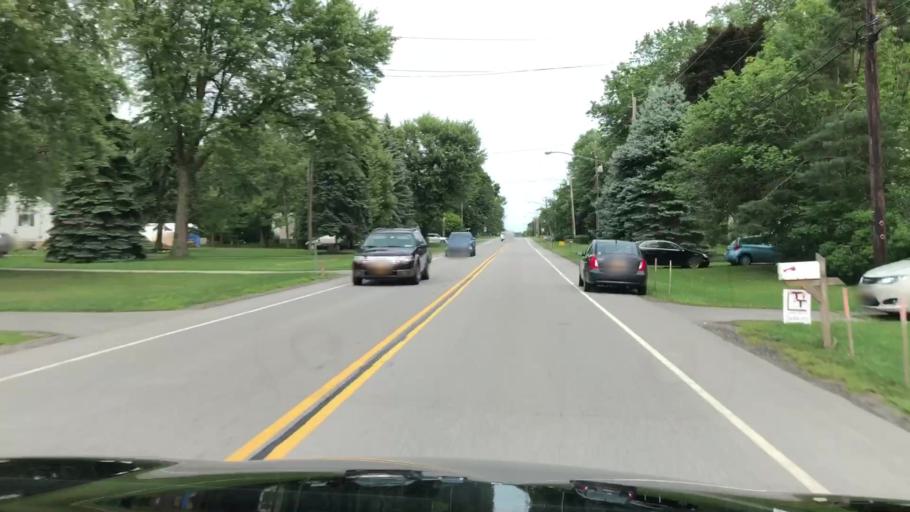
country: US
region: New York
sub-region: Erie County
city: Orchard Park
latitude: 42.7964
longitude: -78.7695
